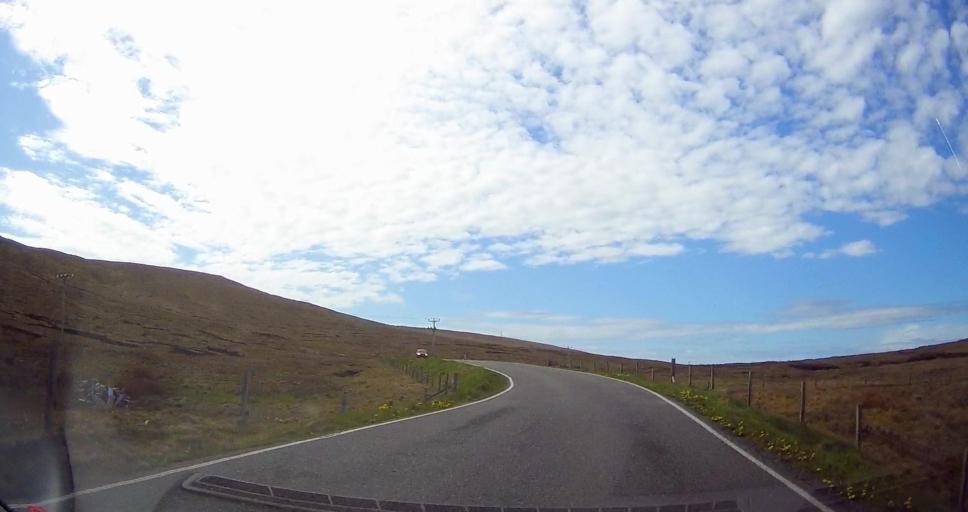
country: GB
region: Scotland
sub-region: Shetland Islands
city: Sandwick
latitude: 59.9833
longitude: -1.2913
